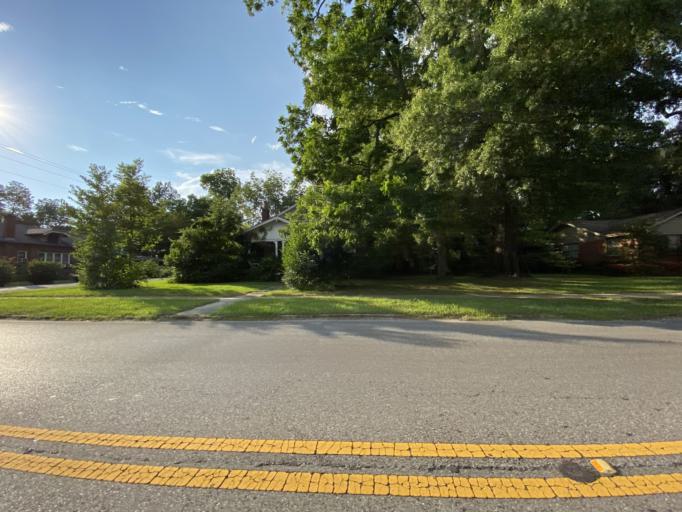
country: US
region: Alabama
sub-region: Morgan County
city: Hartselle
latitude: 34.4455
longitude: -86.9283
